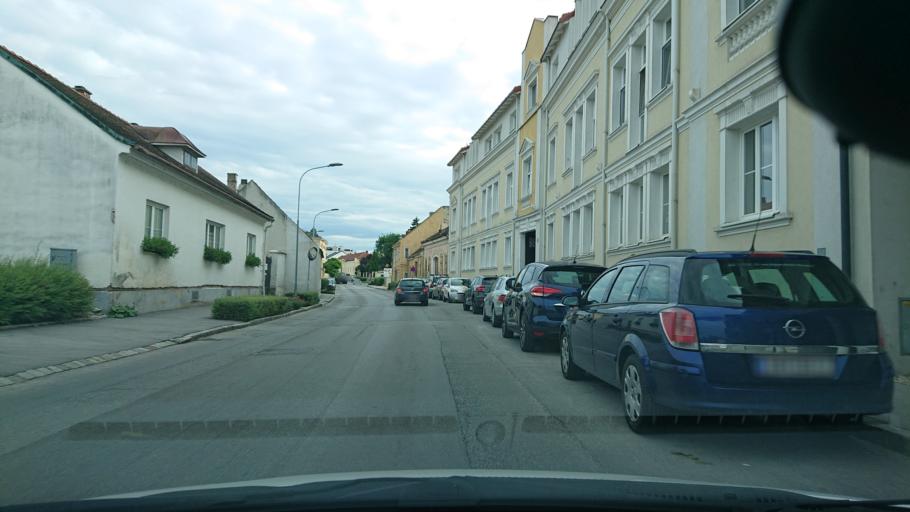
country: AT
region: Lower Austria
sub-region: Politischer Bezirk Baden
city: Leobersdorf
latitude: 47.9252
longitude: 16.2153
